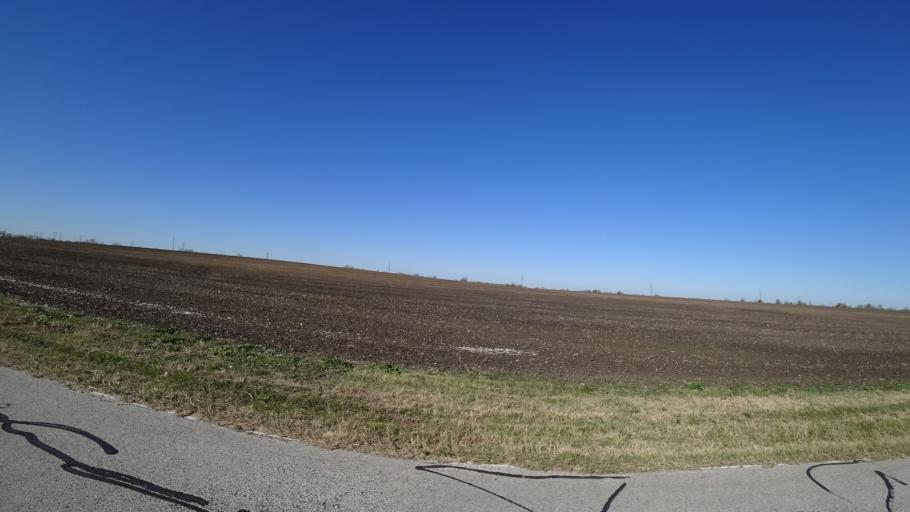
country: US
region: Texas
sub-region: Travis County
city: Garfield
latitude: 30.1041
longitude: -97.6546
